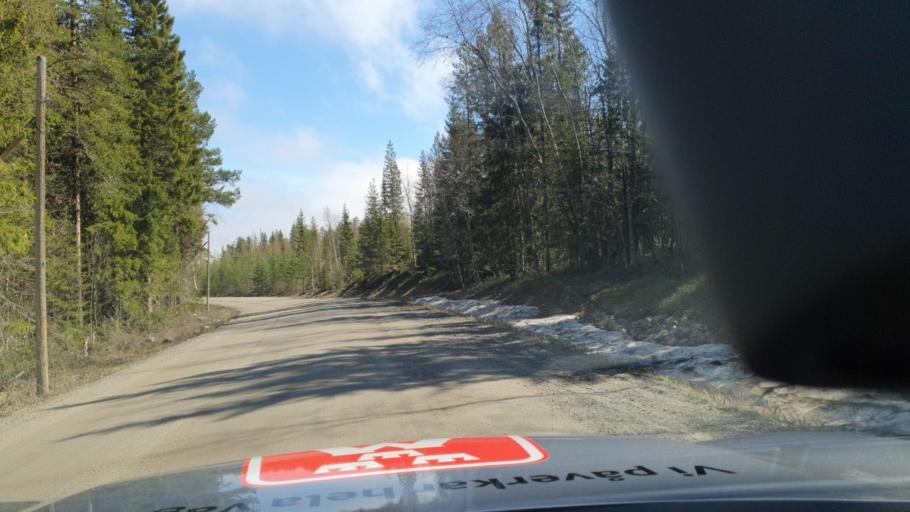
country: SE
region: Vaesterbotten
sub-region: Bjurholms Kommun
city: Bjurholm
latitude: 63.6842
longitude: 18.9730
